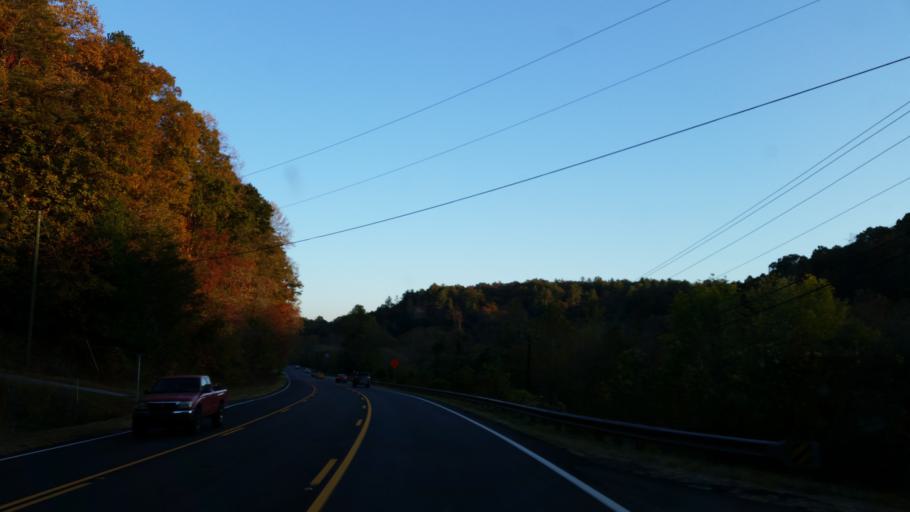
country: US
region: Georgia
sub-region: Lumpkin County
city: Dahlonega
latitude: 34.4736
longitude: -83.9787
